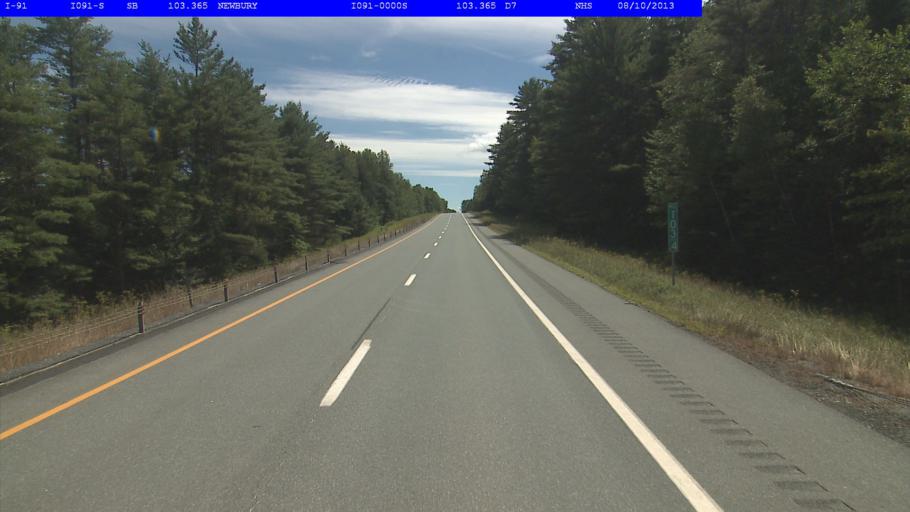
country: US
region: New Hampshire
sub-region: Grafton County
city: Haverhill
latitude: 44.0623
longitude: -72.1096
